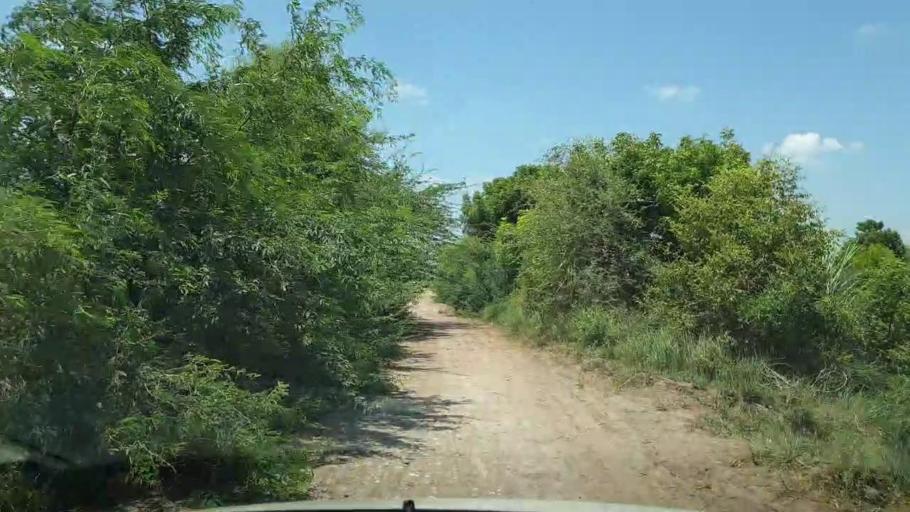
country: PK
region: Sindh
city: Sanghar
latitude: 26.0720
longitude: 69.0478
